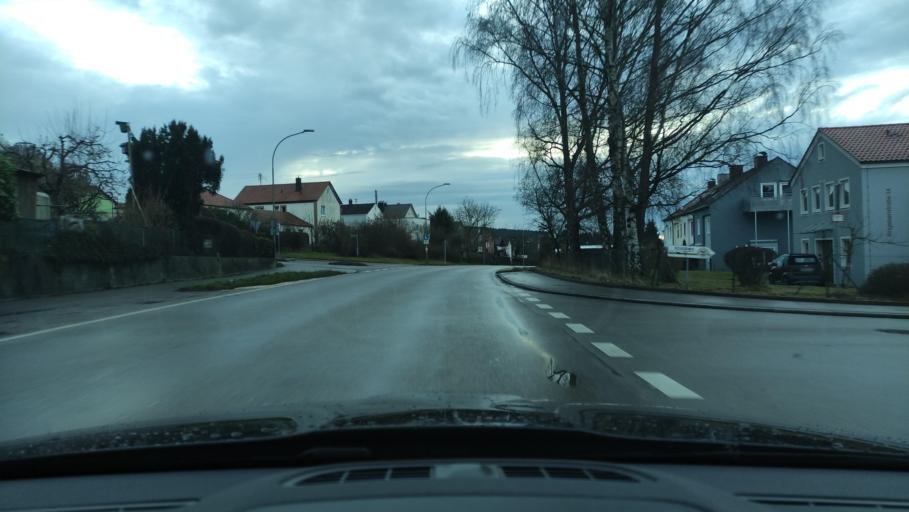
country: DE
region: Bavaria
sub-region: Swabia
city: Krumbach
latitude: 48.2534
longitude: 10.3663
